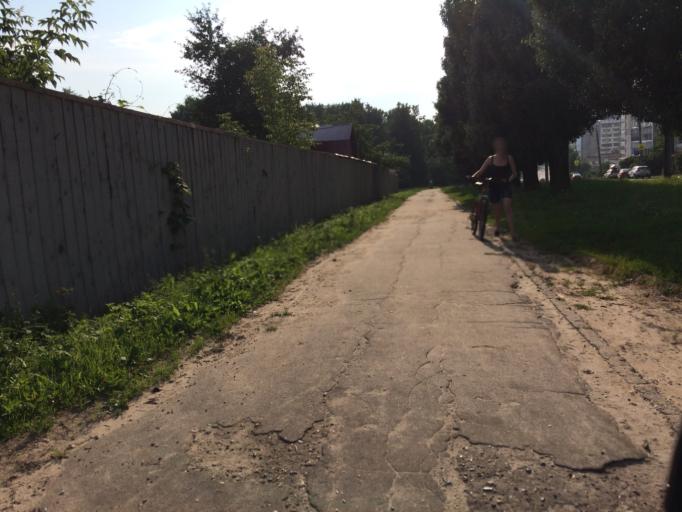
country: RU
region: Mariy-El
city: Yoshkar-Ola
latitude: 56.6216
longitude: 47.9453
